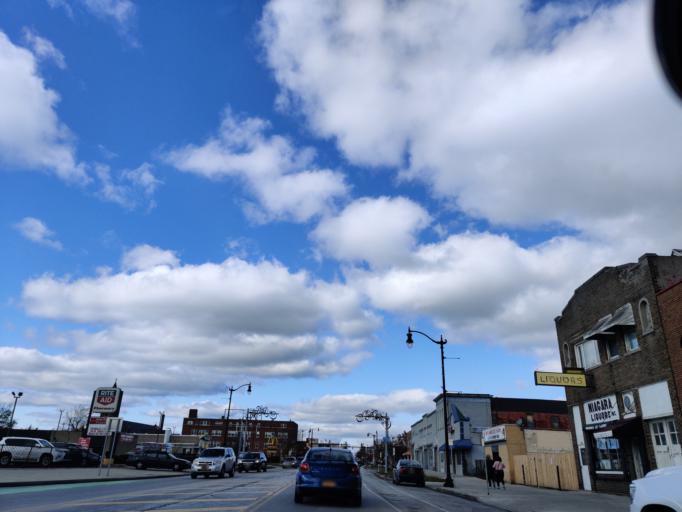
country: US
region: New York
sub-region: Erie County
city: Buffalo
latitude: 42.8937
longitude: -78.8849
